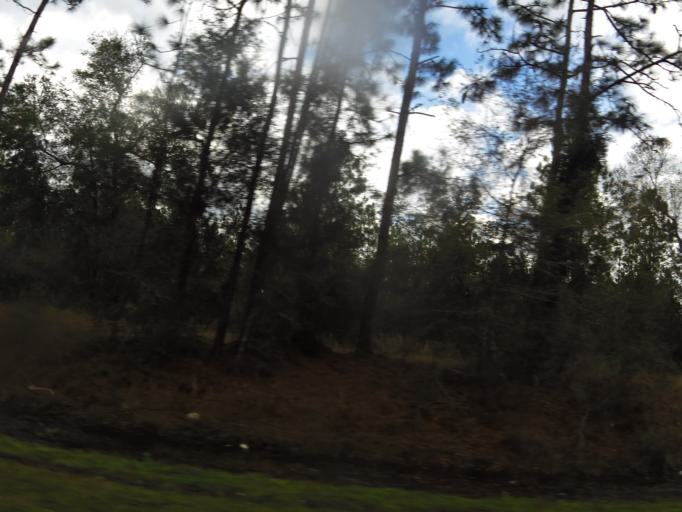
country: US
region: Florida
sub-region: Volusia County
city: Pierson
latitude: 29.2689
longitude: -81.4735
